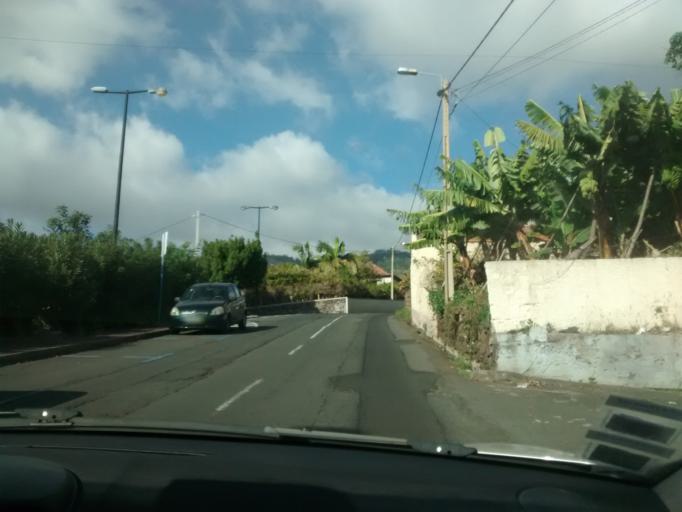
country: PT
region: Madeira
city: Calheta
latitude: 32.7274
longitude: -17.1795
